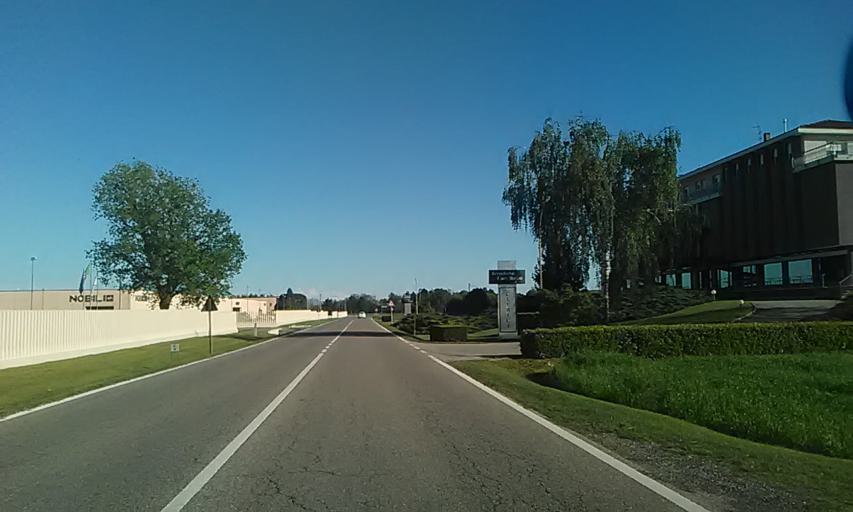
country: IT
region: Piedmont
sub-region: Provincia di Novara
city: Cavaglietto
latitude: 45.6088
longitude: 8.5228
